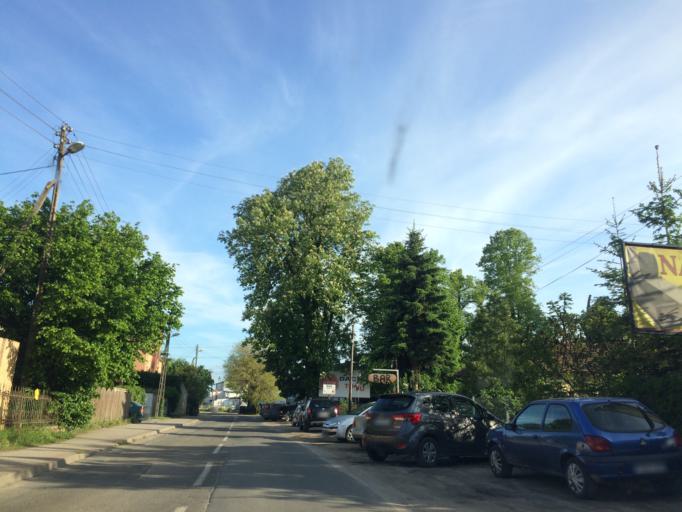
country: PL
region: Lower Silesian Voivodeship
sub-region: Powiat swidnicki
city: Swidnica
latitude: 50.8257
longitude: 16.4890
